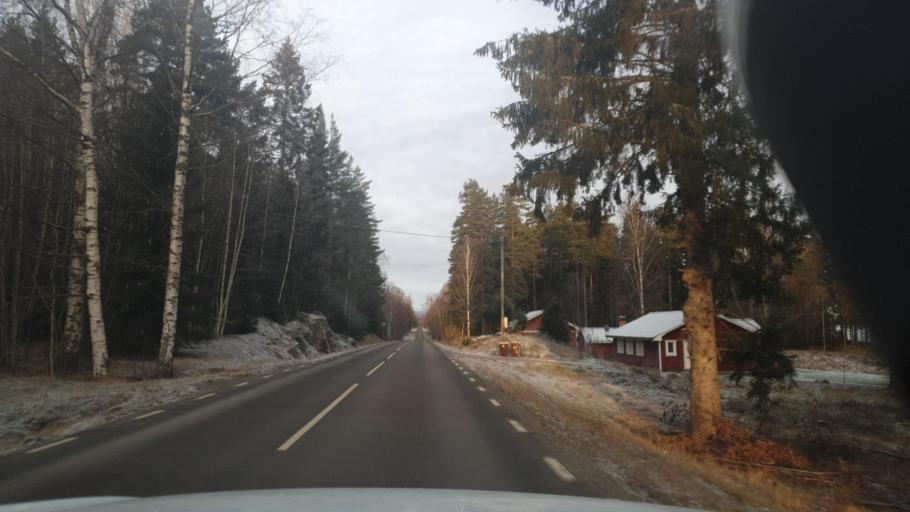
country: SE
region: Vaermland
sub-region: Arvika Kommun
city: Arvika
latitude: 59.6249
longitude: 12.5014
